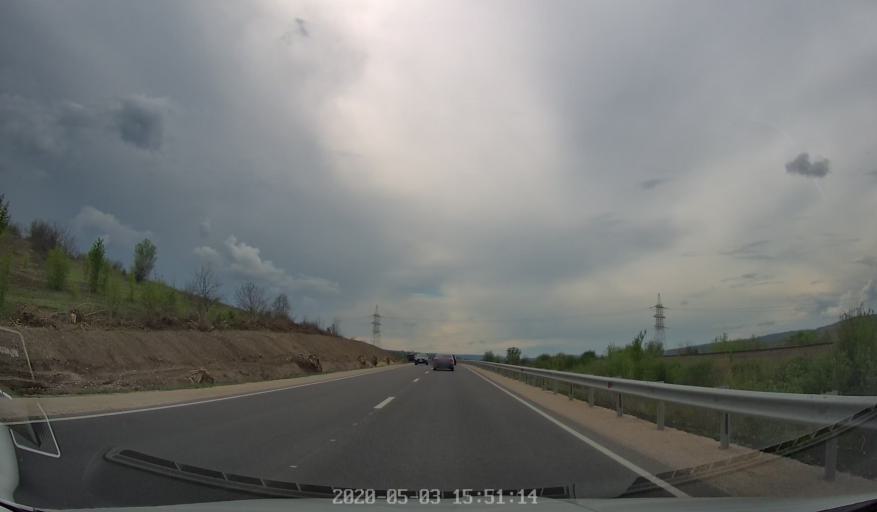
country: MD
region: Straseni
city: Straseni
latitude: 47.1608
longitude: 28.5628
